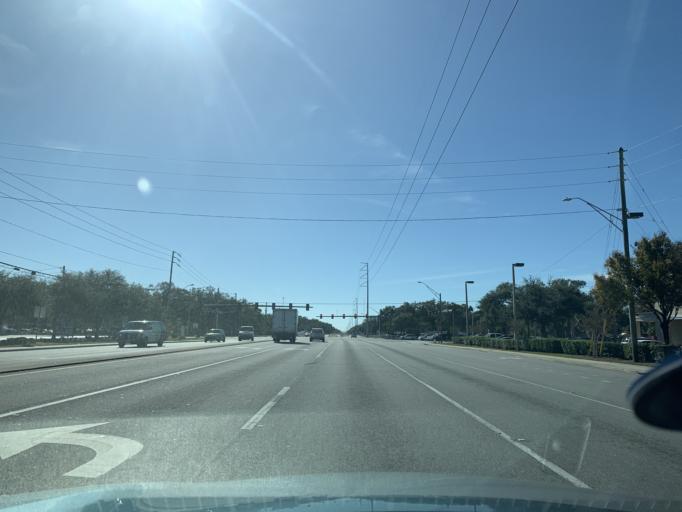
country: US
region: Florida
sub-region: Pinellas County
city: Seminole
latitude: 27.8736
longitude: -82.7624
